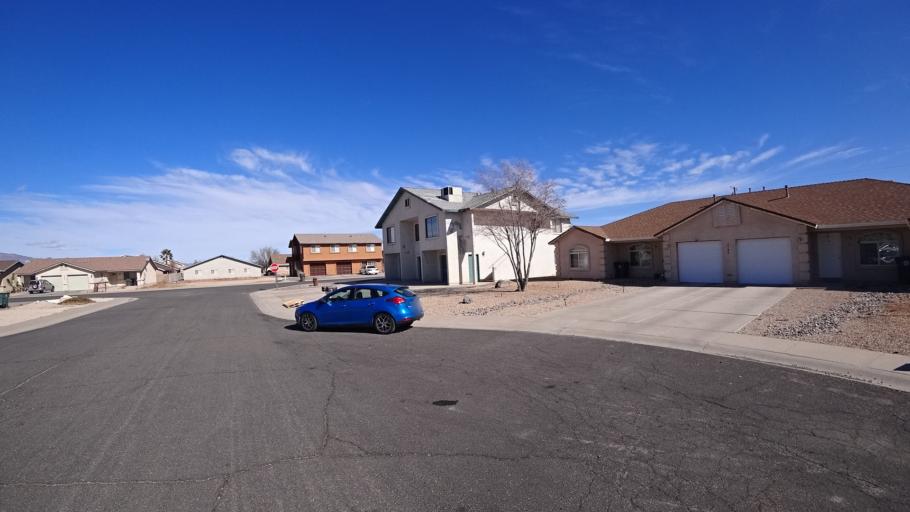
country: US
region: Arizona
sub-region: Mohave County
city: Kingman
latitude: 35.2199
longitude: -114.0212
